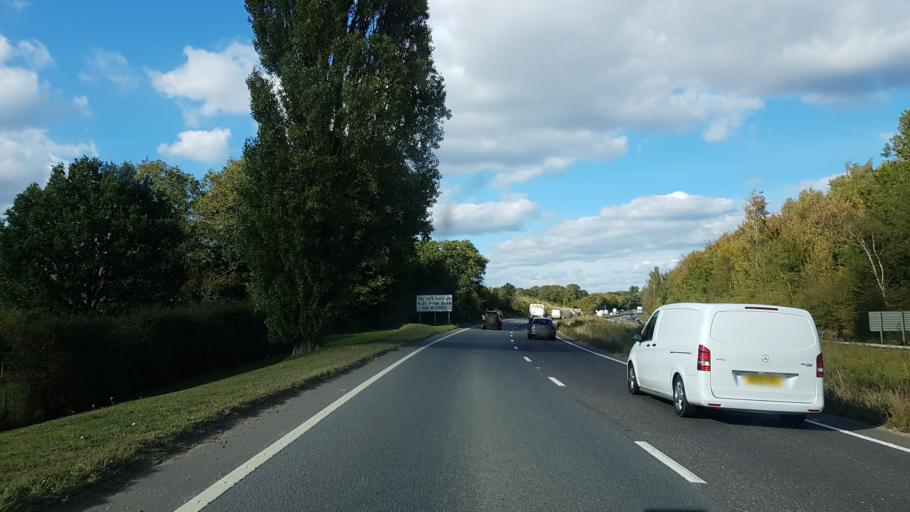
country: GB
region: England
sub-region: Surrey
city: Milford
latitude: 51.2047
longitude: -0.6507
